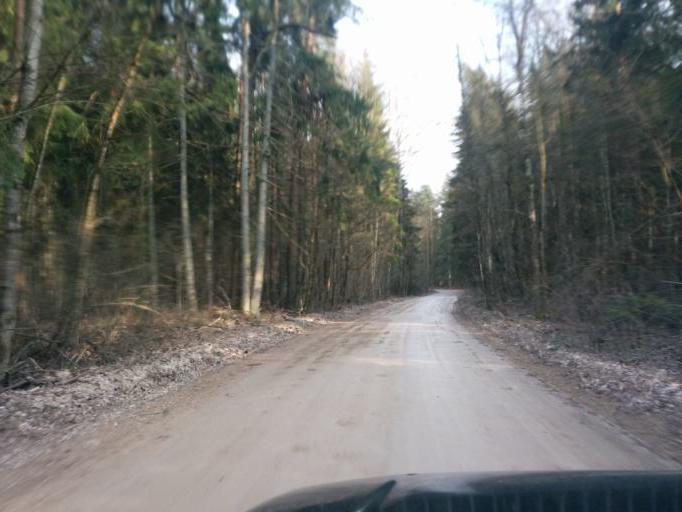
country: LV
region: Olaine
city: Olaine
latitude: 56.7902
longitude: 24.0329
